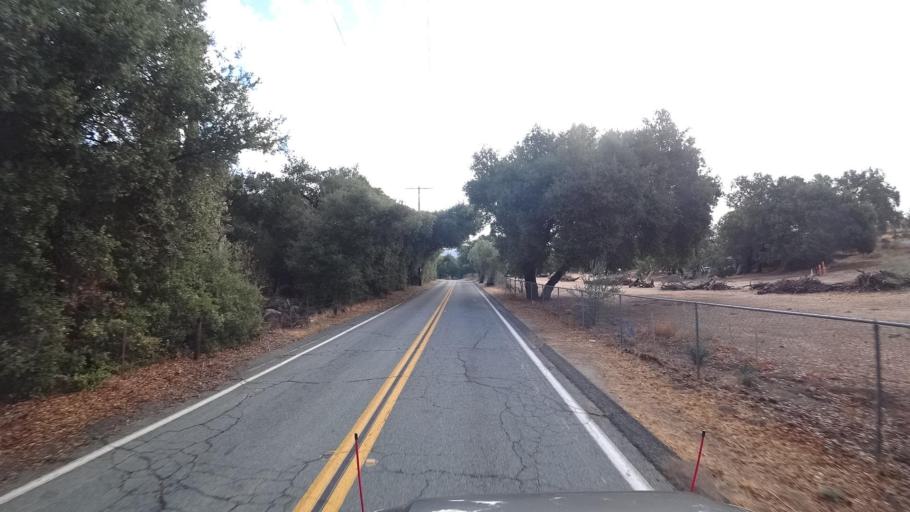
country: MX
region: Baja California
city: Tecate
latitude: 32.6262
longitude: -116.5993
